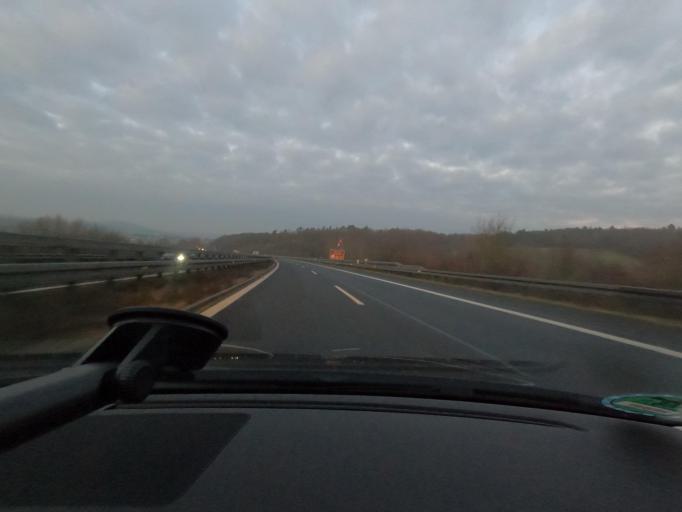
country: DE
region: Bavaria
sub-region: Upper Franconia
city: Ebensfeld
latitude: 50.0374
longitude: 10.9581
